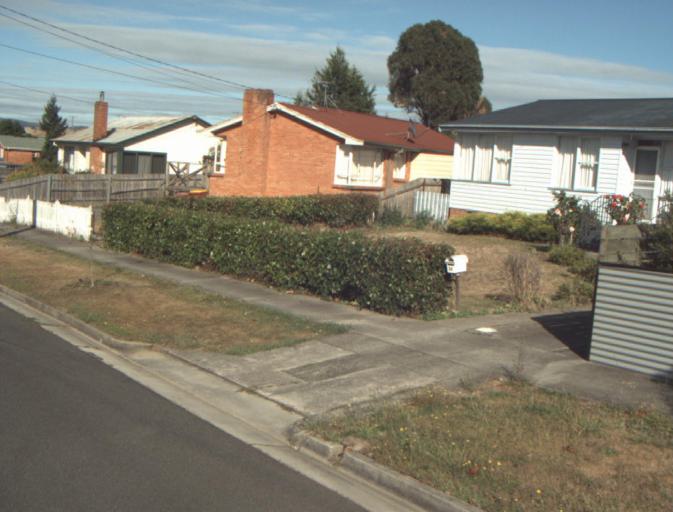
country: AU
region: Tasmania
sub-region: Launceston
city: Mayfield
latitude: -41.3894
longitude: 147.1330
